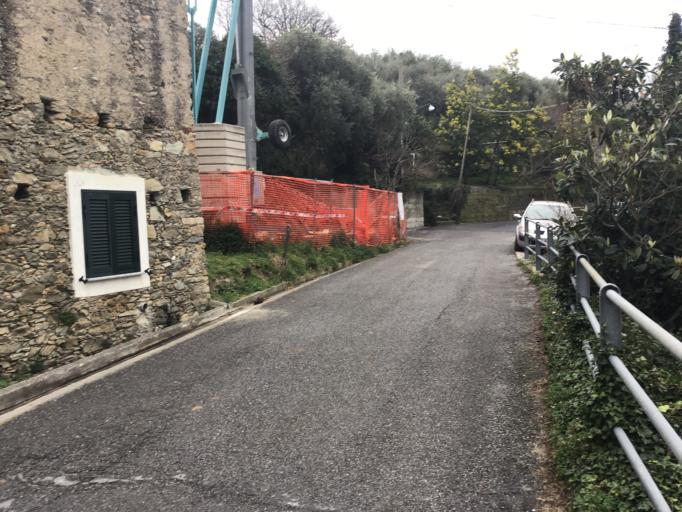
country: IT
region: Liguria
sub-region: Provincia di Savona
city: Orco Feglino
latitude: 44.2235
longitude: 8.3239
